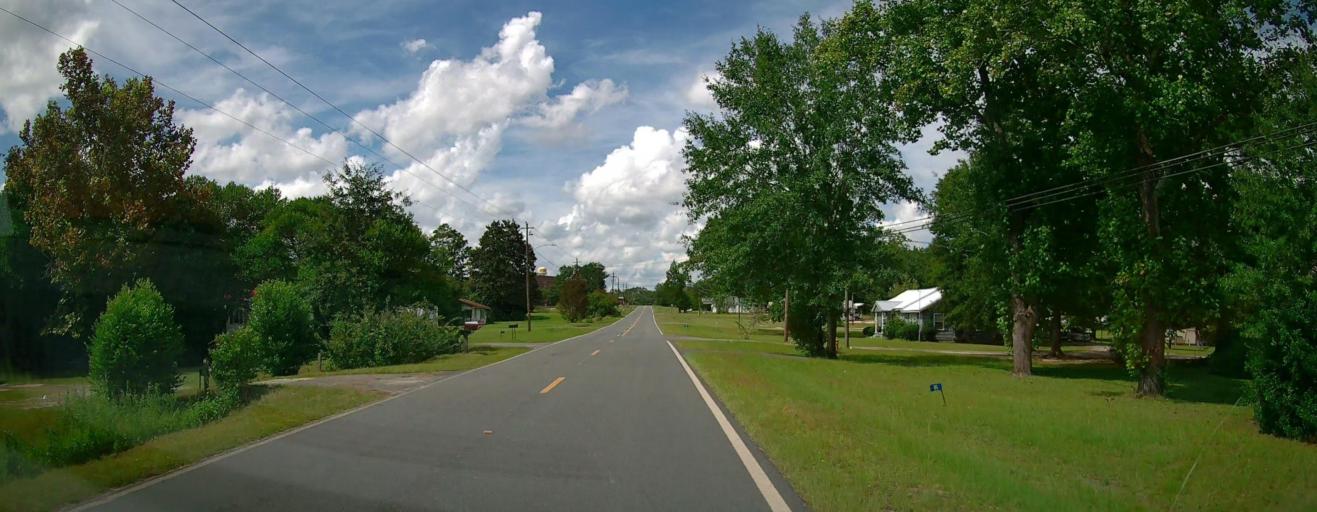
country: US
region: Georgia
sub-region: Taylor County
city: Butler
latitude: 32.5503
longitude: -84.2297
